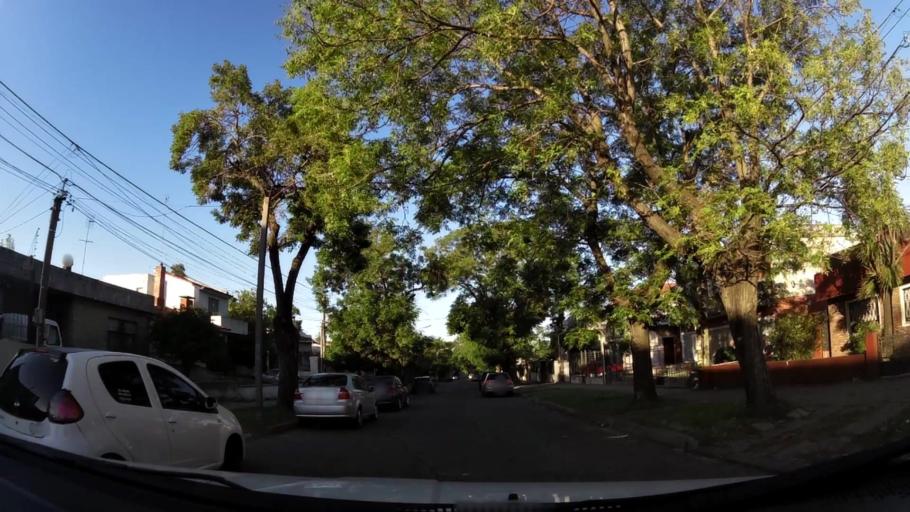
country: UY
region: Montevideo
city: Montevideo
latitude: -34.8433
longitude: -56.2059
